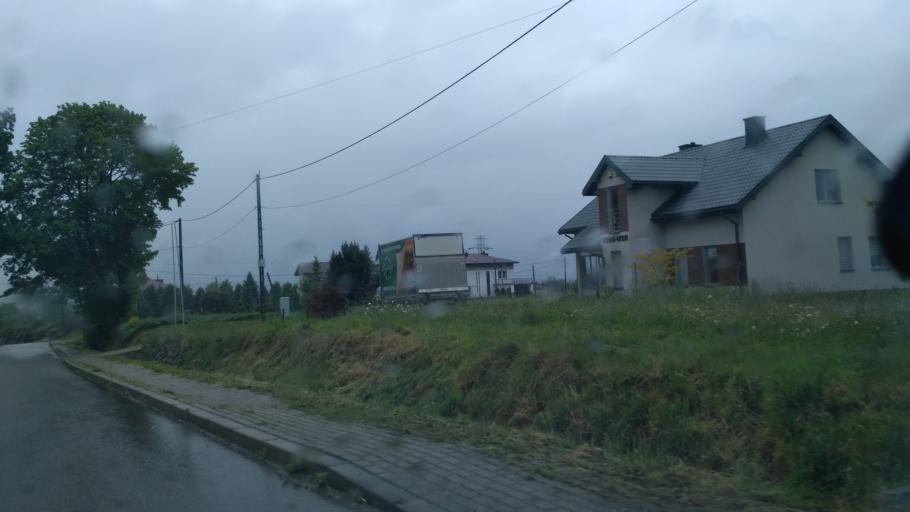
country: PL
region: Subcarpathian Voivodeship
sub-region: Powiat jasielski
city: Tarnowiec
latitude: 49.7634
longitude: 21.5400
